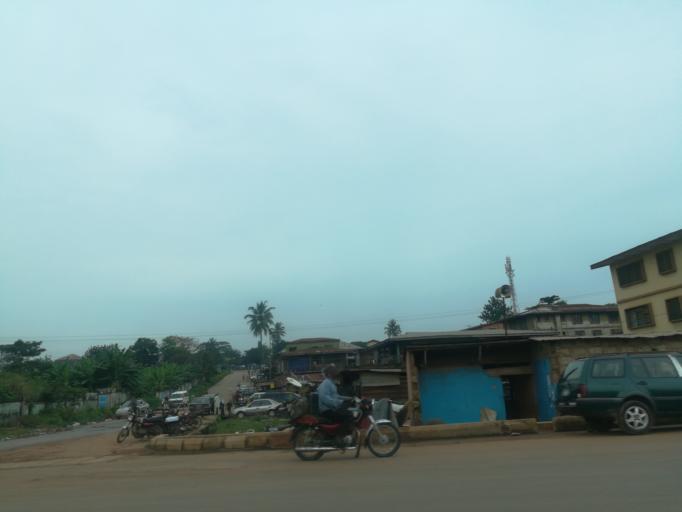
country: NG
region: Oyo
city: Ibadan
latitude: 7.3970
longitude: 3.9228
